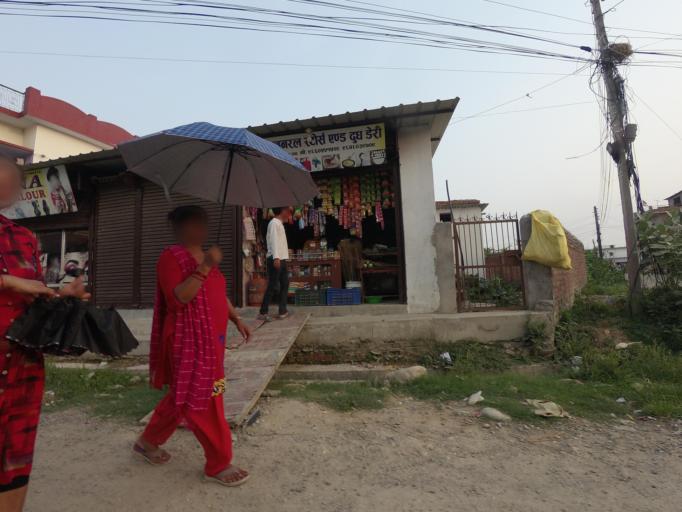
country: NP
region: Western Region
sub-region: Lumbini Zone
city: Bhairahawa
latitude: 27.5176
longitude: 83.4582
